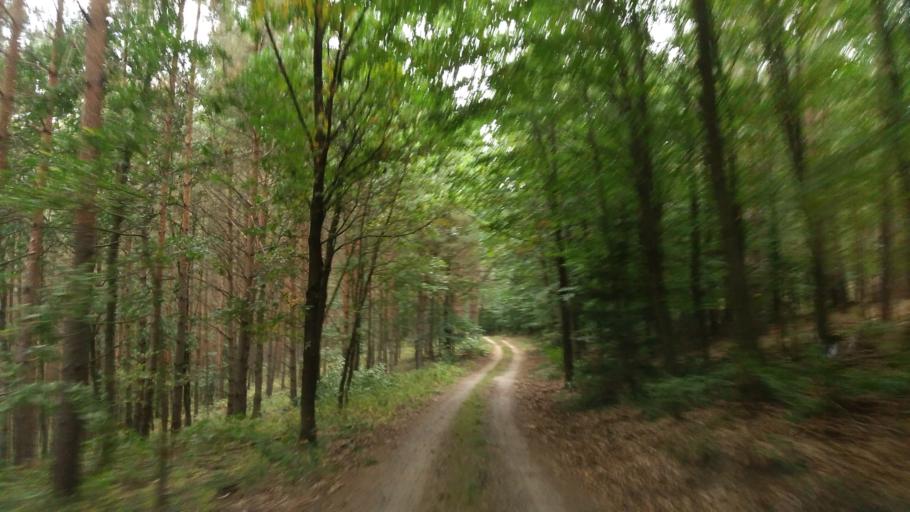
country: PL
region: West Pomeranian Voivodeship
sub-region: Powiat choszczenski
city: Bierzwnik
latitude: 52.9798
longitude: 15.6142
